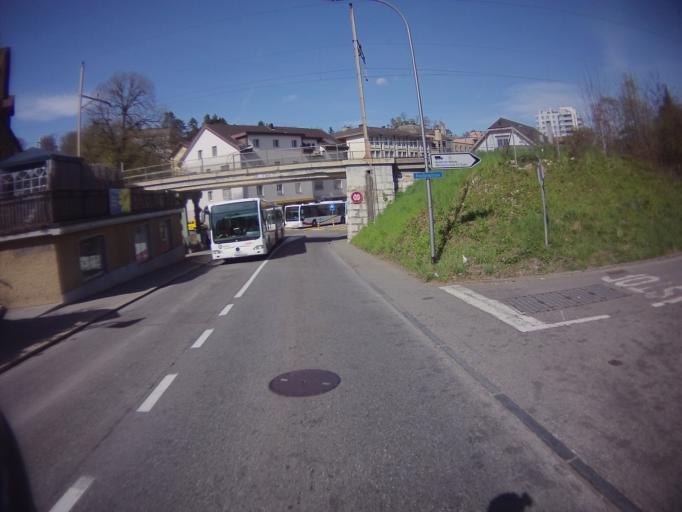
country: CH
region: Aargau
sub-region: Bezirk Baden
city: Baden
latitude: 47.4698
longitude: 8.3024
